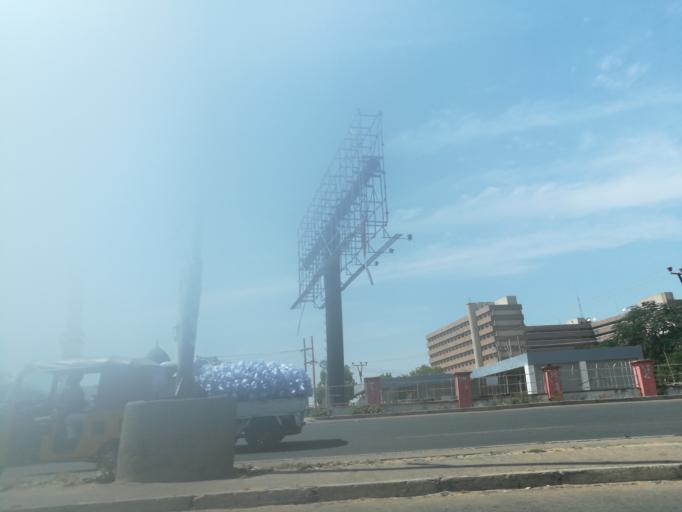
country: NG
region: Kano
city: Kano
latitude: 12.0236
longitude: 8.5158
